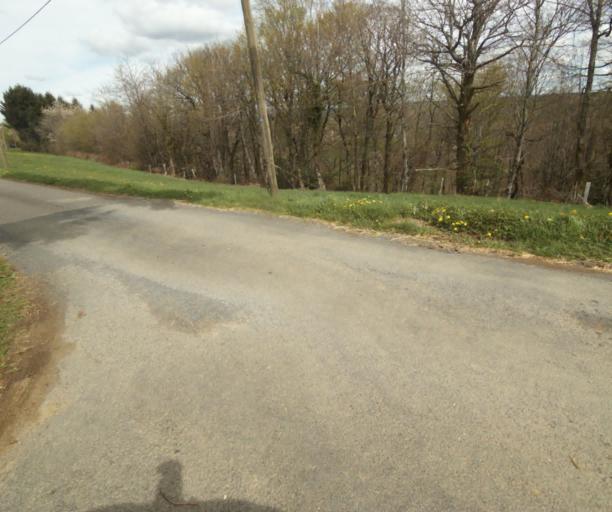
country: FR
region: Limousin
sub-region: Departement de la Correze
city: Laguenne
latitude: 45.2169
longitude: 1.8503
